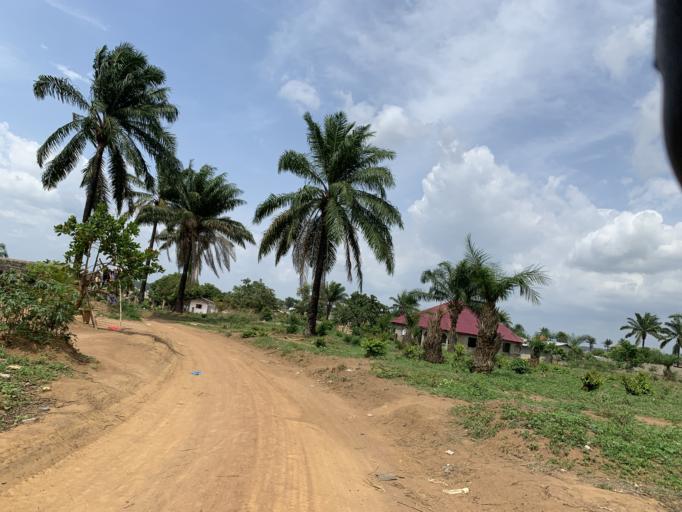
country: SL
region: Western Area
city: Waterloo
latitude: 8.3549
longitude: -13.0442
